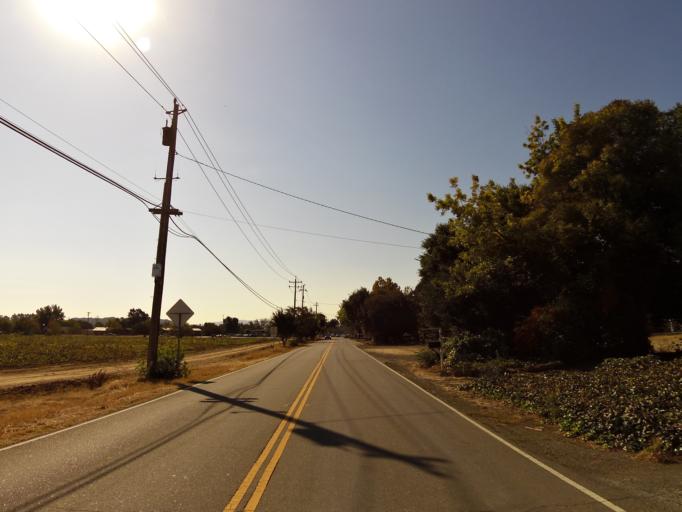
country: US
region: California
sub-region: Solano County
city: Green Valley
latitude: 38.2465
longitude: -122.1213
